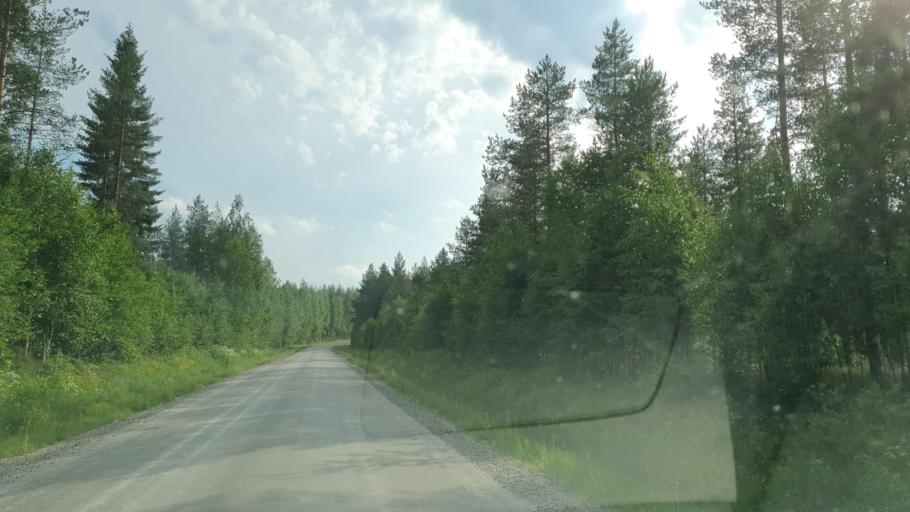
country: FI
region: Kainuu
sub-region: Kehys-Kainuu
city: Kuhmo
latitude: 64.0930
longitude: 29.6036
